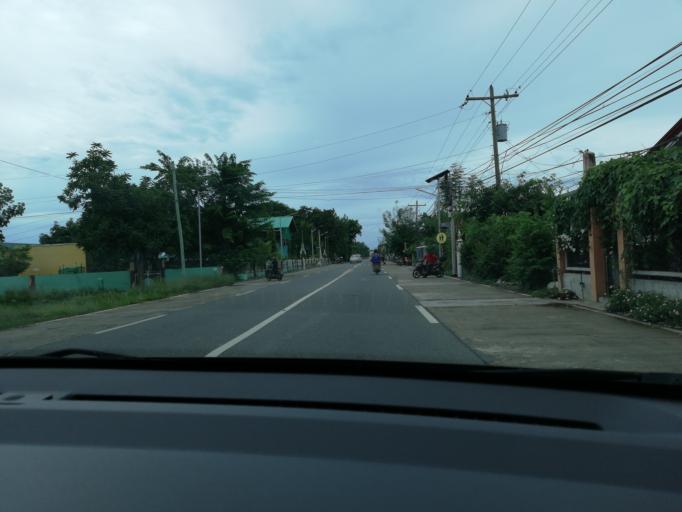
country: PH
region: Ilocos
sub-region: Province of Ilocos Sur
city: San Vicente
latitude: 17.5844
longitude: 120.3716
